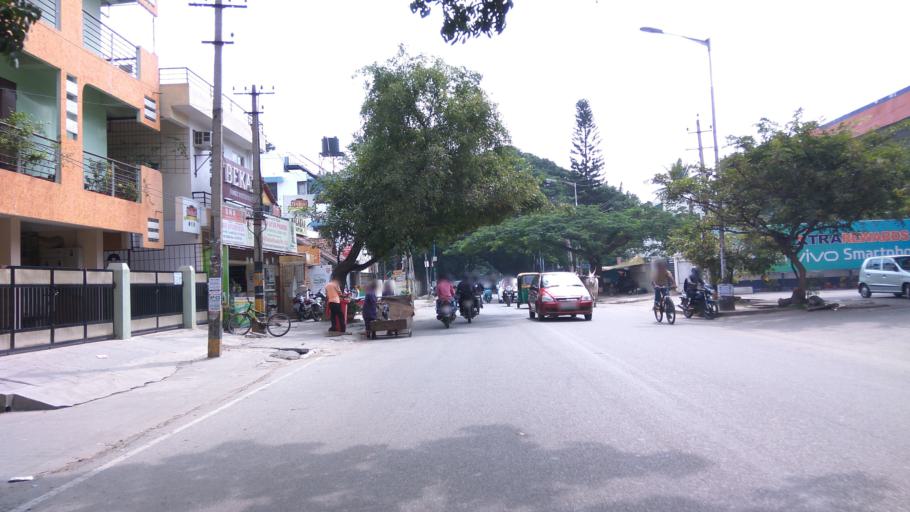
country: IN
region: Karnataka
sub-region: Bangalore Urban
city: Bangalore
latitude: 12.9677
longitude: 77.6541
